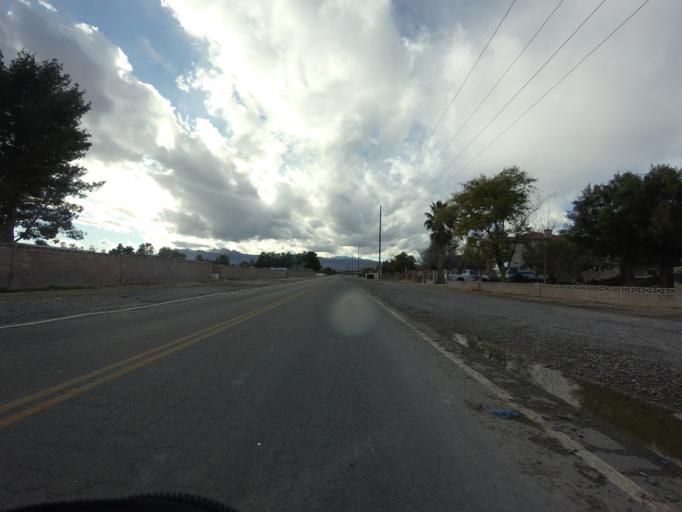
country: US
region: Nevada
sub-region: Clark County
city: Las Vegas
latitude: 36.2690
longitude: -115.2340
